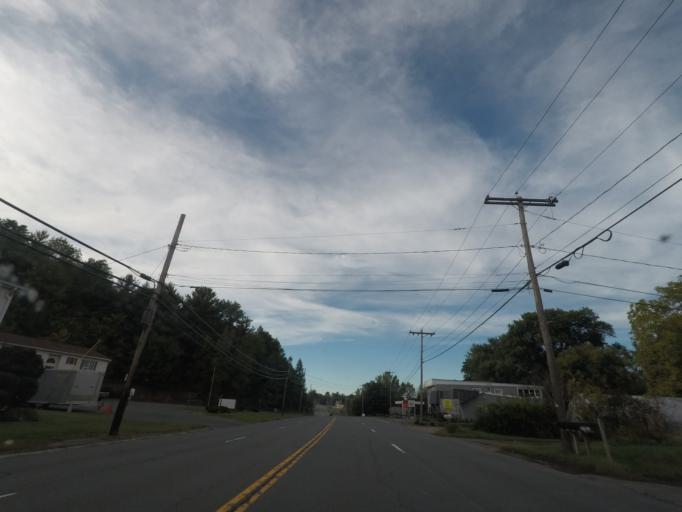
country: US
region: New York
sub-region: Rensselaer County
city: East Greenbush
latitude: 42.5694
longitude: -73.6853
